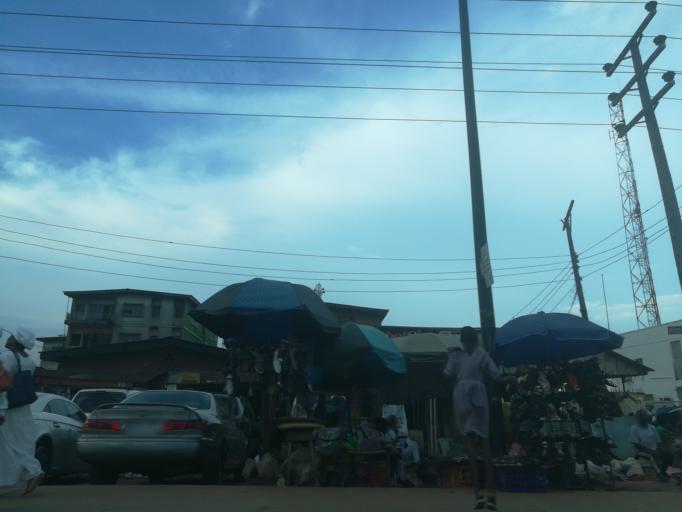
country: NG
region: Lagos
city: Ikorodu
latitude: 6.6232
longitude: 3.4977
